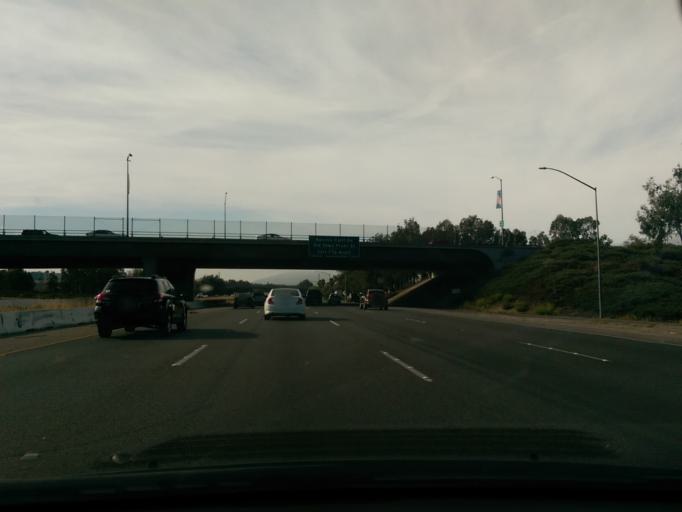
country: US
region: California
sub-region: Riverside County
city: Temecula
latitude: 33.5231
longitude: -117.1636
